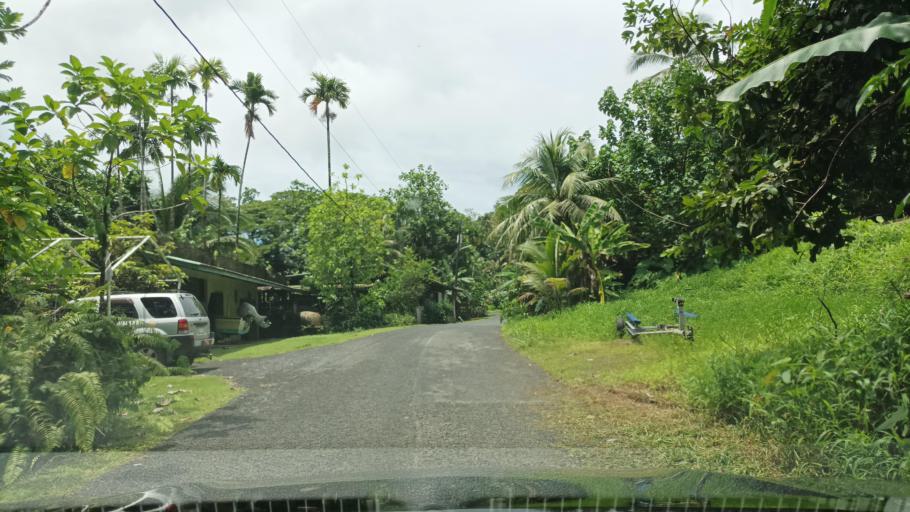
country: FM
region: Pohnpei
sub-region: Kolonia Municipality
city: Kolonia
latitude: 6.9551
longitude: 158.2272
